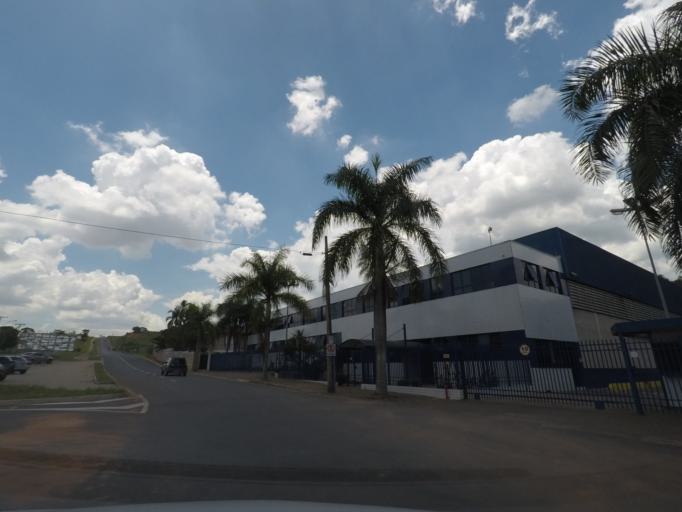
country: BR
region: Sao Paulo
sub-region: Valinhos
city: Valinhos
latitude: -22.9909
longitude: -46.9939
